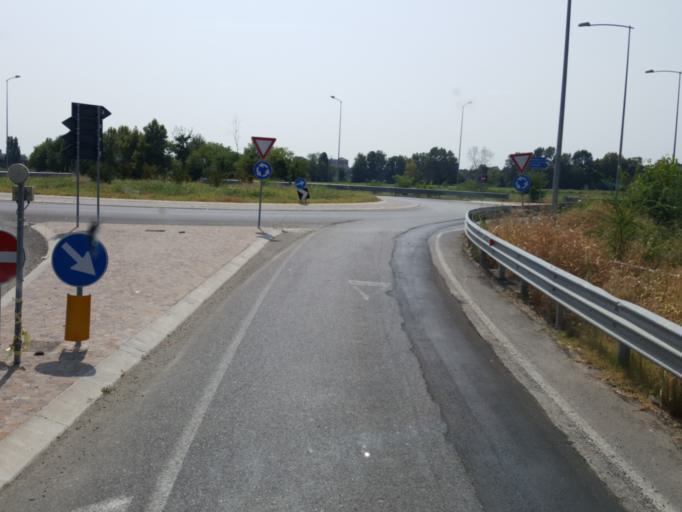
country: IT
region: Lombardy
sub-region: Citta metropolitana di Milano
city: Pozzuolo Martesana
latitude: 45.5122
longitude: 9.4381
